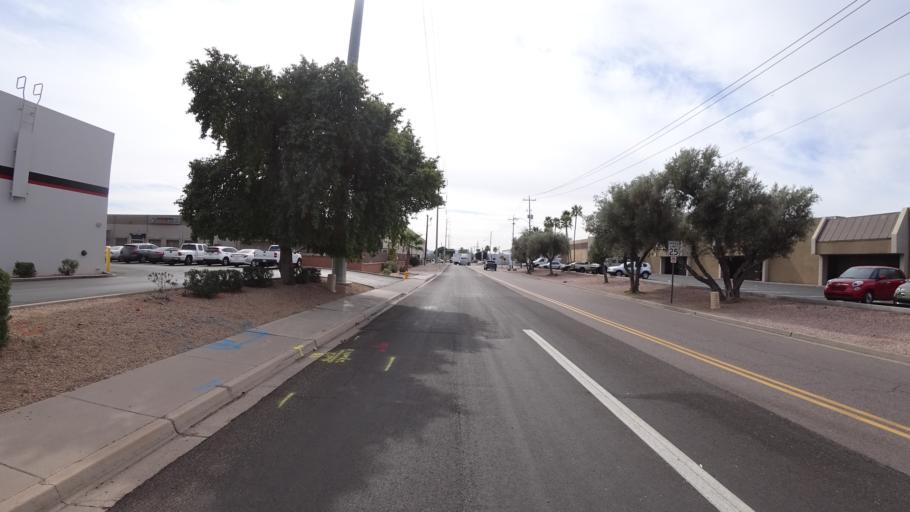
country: US
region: Arizona
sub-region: Maricopa County
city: Phoenix
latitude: 33.4799
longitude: -112.1257
